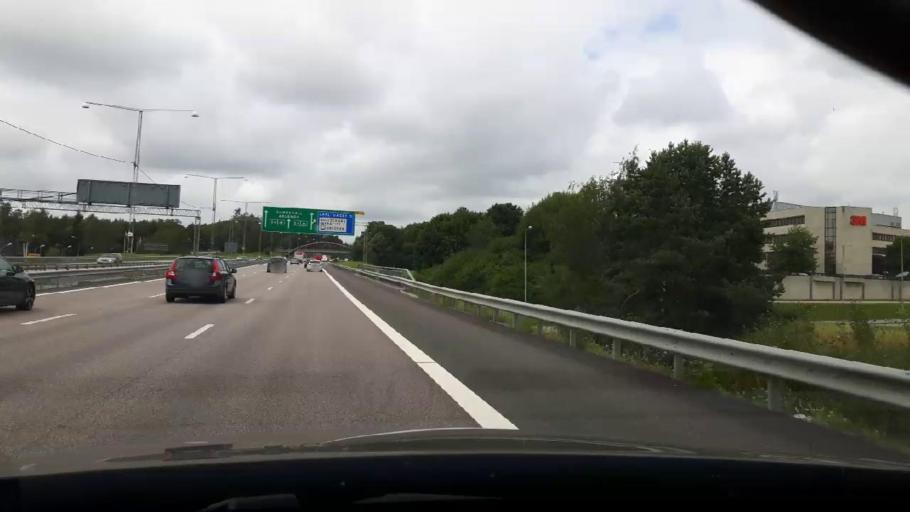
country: SE
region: Stockholm
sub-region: Upplands Vasby Kommun
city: Upplands Vaesby
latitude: 59.4828
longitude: 17.9200
